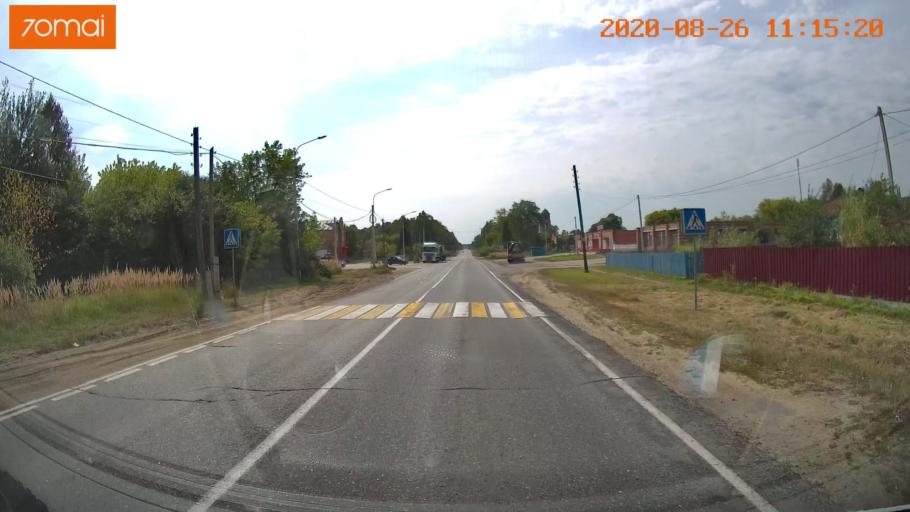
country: RU
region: Rjazan
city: Izhevskoye
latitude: 54.4403
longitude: 41.1149
